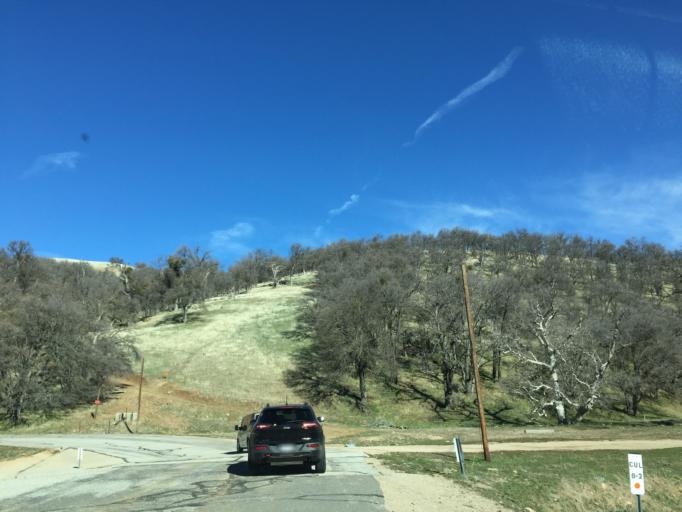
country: US
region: California
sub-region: Kern County
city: Lebec
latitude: 34.8835
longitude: -118.7744
